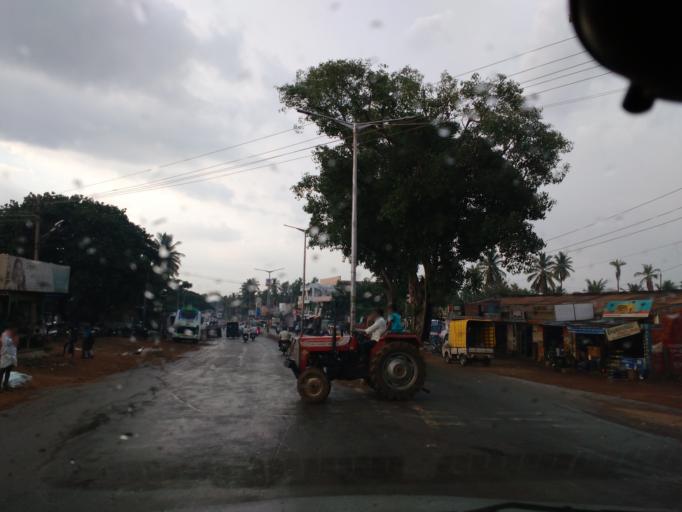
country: IN
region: Karnataka
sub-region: Tumkur
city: Tiptur
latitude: 13.2578
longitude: 76.4838
